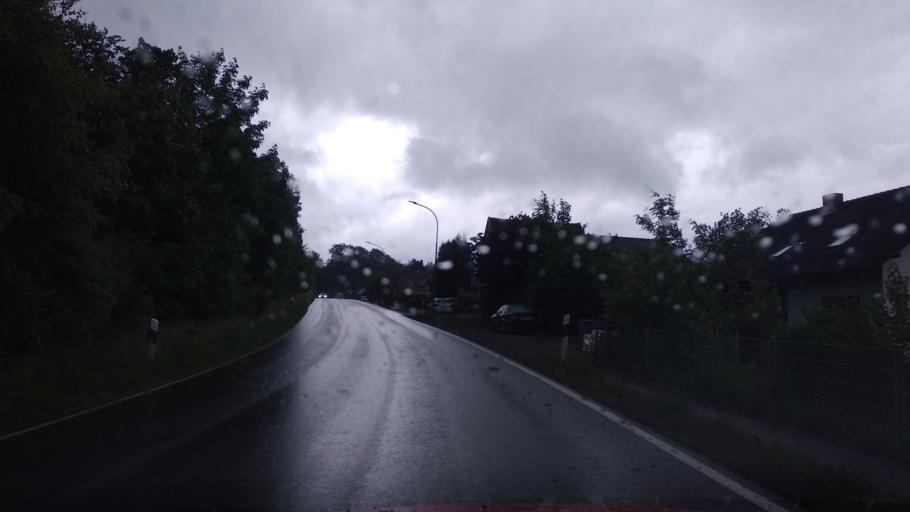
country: DE
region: Lower Saxony
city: Obernkirchen
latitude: 52.2538
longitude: 9.1347
